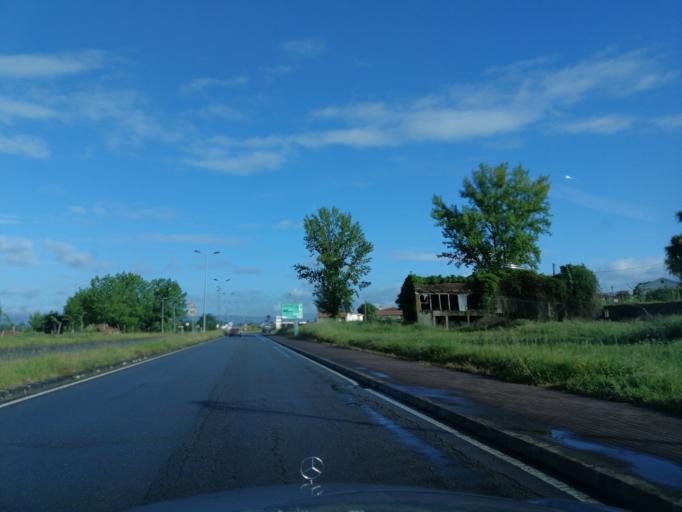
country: PT
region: Braga
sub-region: Braga
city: Braga
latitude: 41.5645
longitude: -8.4380
